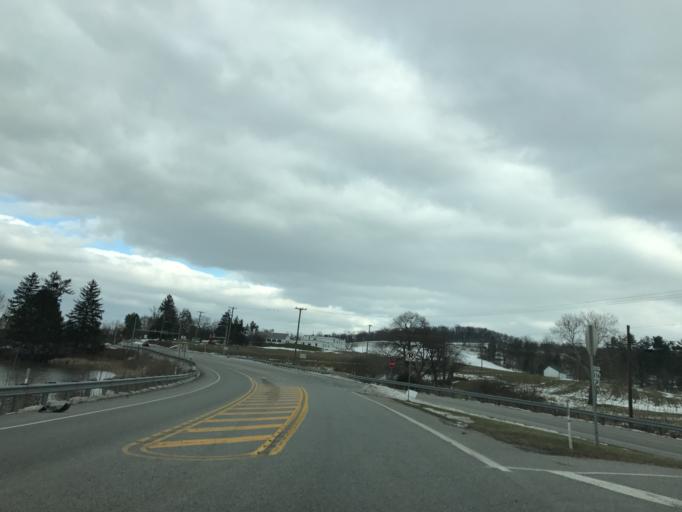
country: US
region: Pennsylvania
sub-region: York County
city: Spring Grove
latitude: 39.8654
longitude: -76.8676
